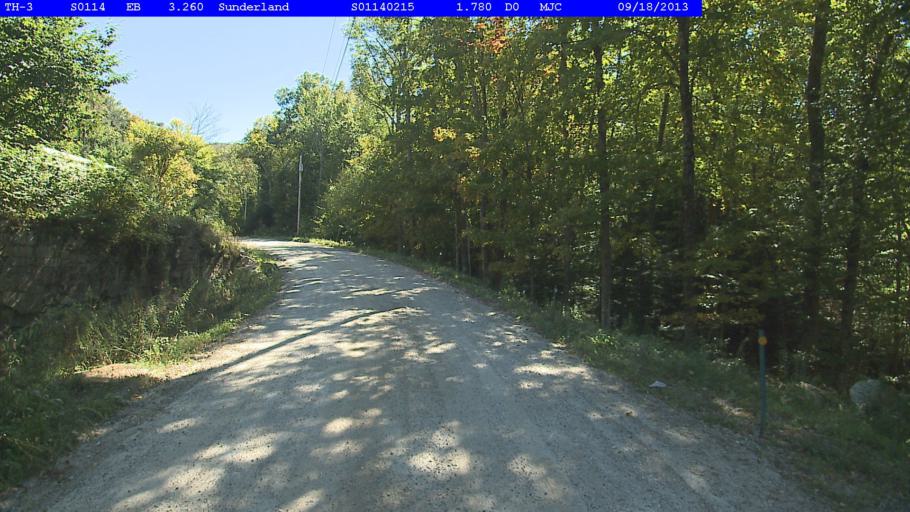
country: US
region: Vermont
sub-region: Bennington County
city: Arlington
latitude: 43.0479
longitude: -73.1166
